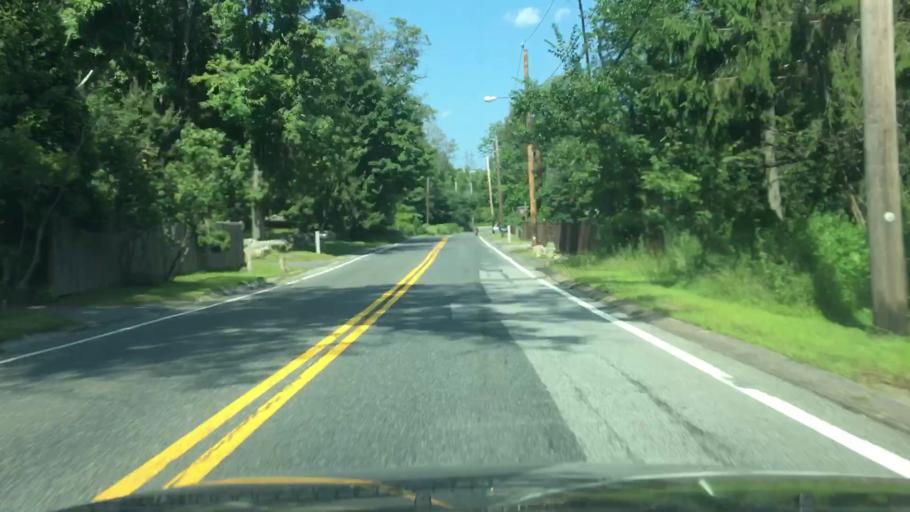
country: US
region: Massachusetts
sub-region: Worcester County
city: Milford
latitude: 42.1670
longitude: -71.4791
